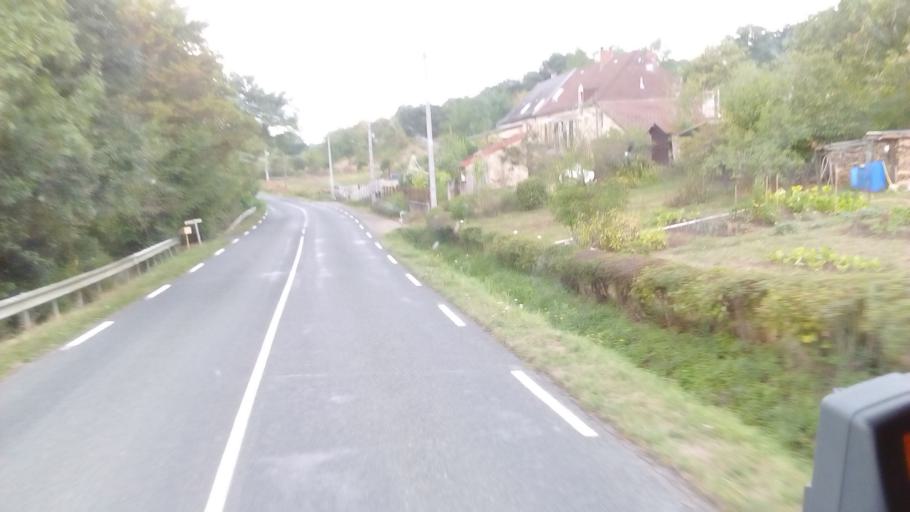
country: FR
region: Bourgogne
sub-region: Departement de Saone-et-Loire
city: La Motte-Saint-Jean
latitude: 46.4936
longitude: 3.9483
